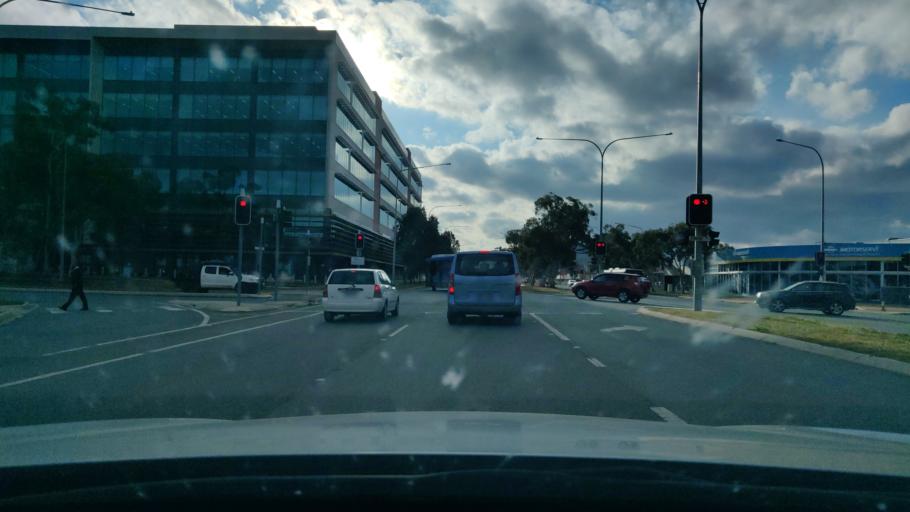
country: AU
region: Australian Capital Territory
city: Macarthur
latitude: -35.4203
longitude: 149.0657
